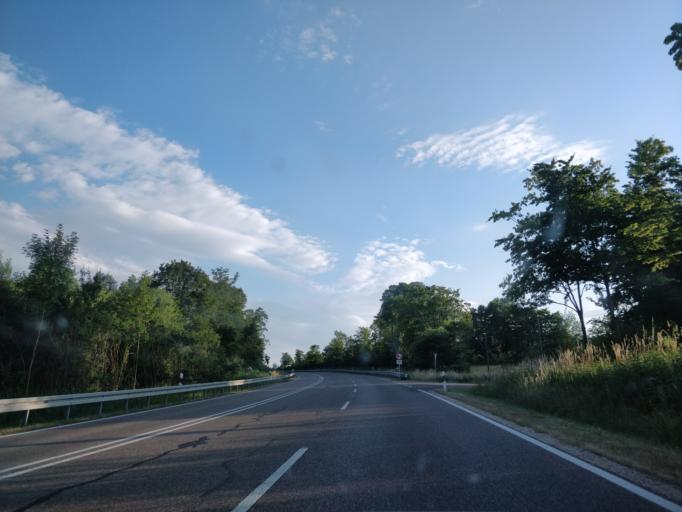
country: DE
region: Bavaria
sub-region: Swabia
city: Ederheim
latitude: 48.8200
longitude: 10.4589
